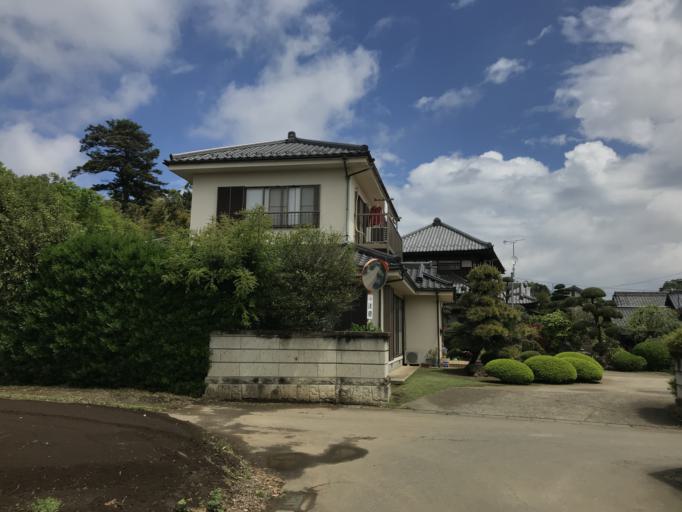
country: JP
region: Ibaraki
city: Moriya
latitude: 35.9542
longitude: 139.9570
